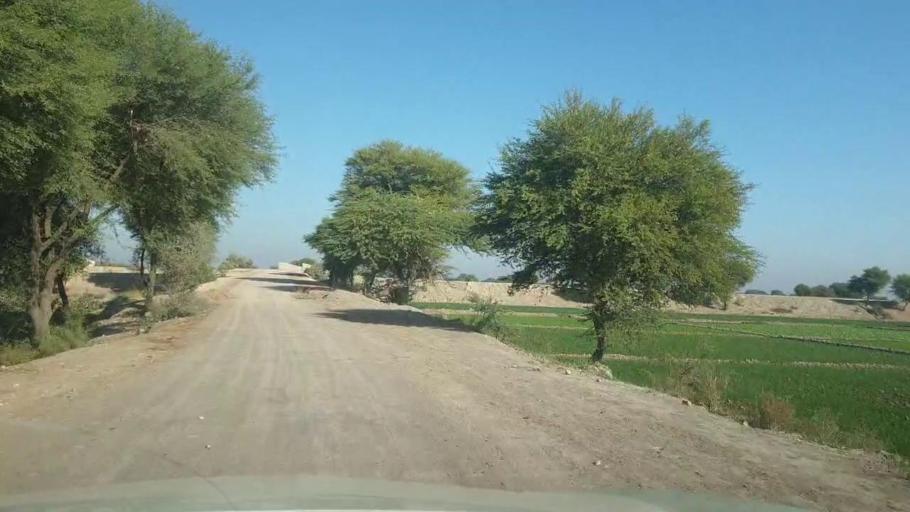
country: PK
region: Sindh
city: Bhan
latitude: 26.5573
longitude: 67.6641
